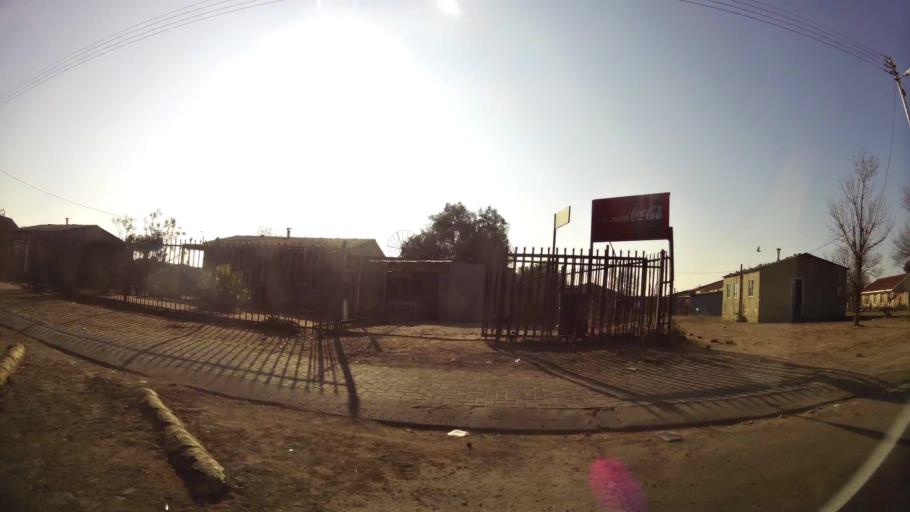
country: ZA
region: Orange Free State
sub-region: Mangaung Metropolitan Municipality
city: Bloemfontein
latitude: -29.1544
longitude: 26.2534
